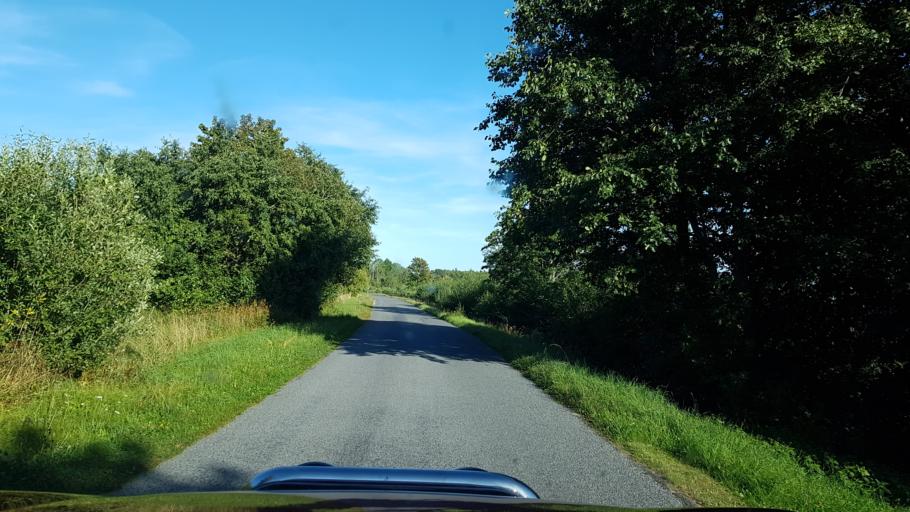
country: LV
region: Salacgrivas
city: Ainazi
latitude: 57.8766
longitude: 24.3661
